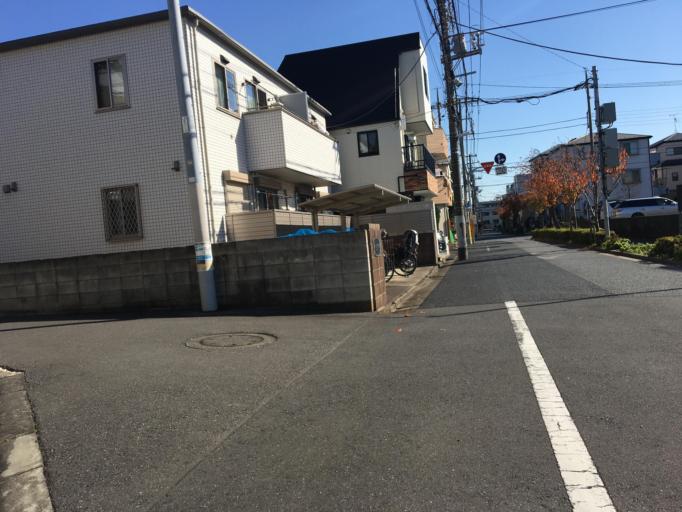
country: JP
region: Tokyo
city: Urayasu
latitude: 35.6998
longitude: 139.9103
